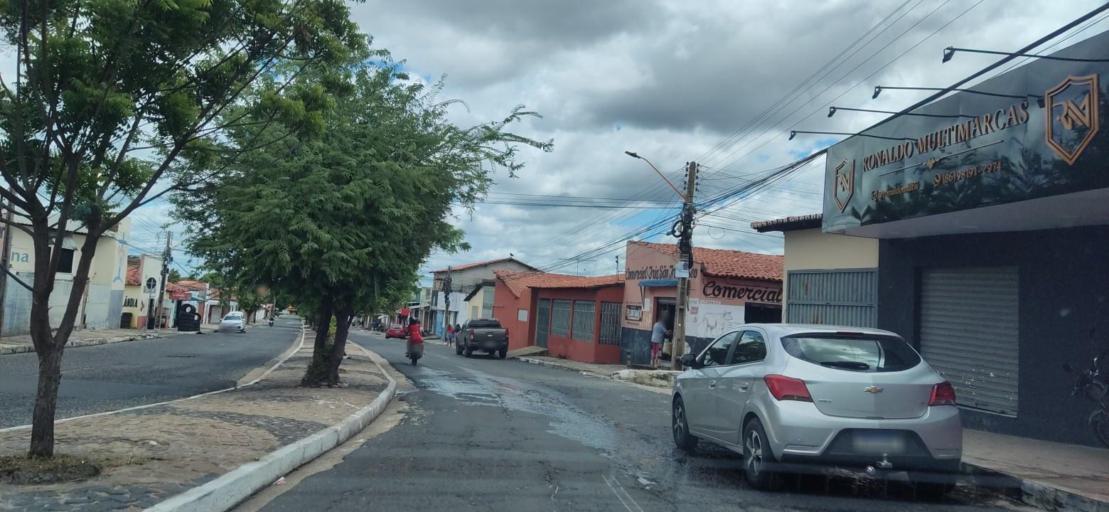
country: BR
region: Piaui
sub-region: Teresina
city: Teresina
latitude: -5.1453
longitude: -42.7793
